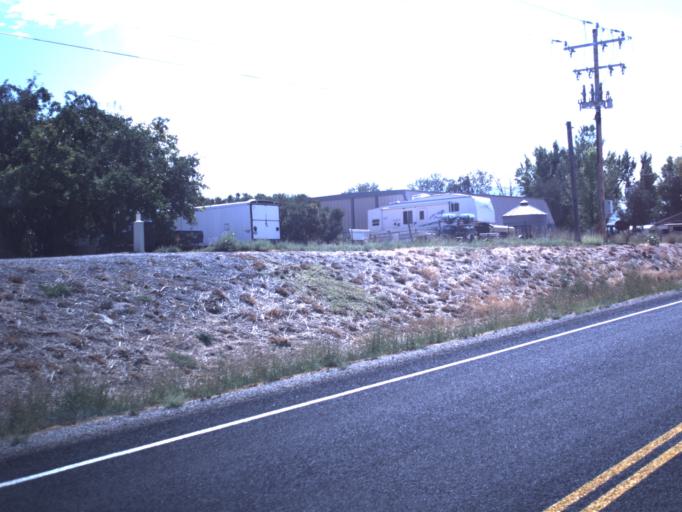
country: US
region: Utah
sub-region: Box Elder County
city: Garland
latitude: 41.8297
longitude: -112.1457
